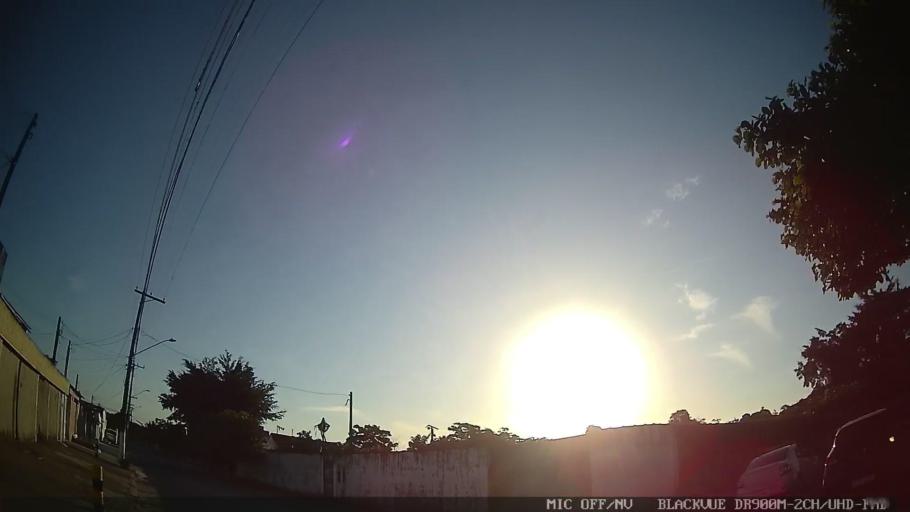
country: BR
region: Sao Paulo
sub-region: Guaruja
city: Guaruja
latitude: -23.9696
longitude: -46.2759
